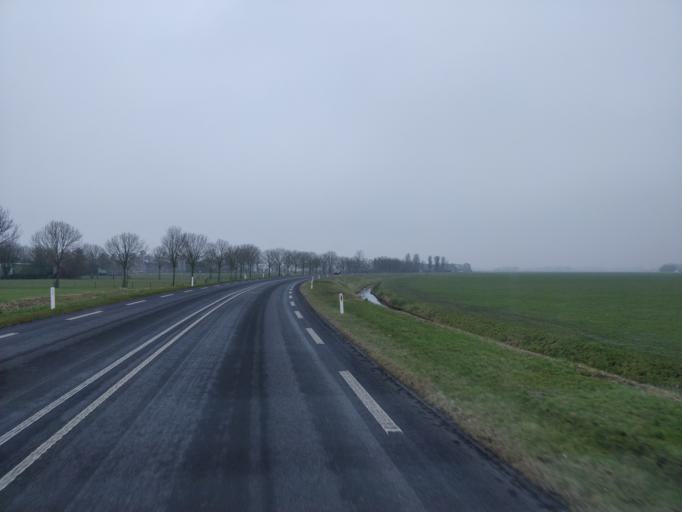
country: NL
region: Friesland
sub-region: Menameradiel
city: Berltsum
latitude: 53.2422
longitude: 5.6652
